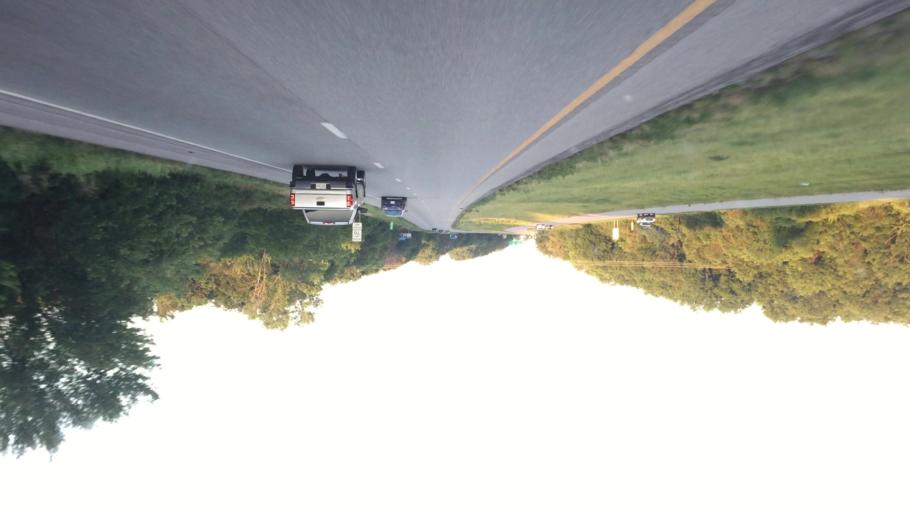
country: US
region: Missouri
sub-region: Clay County
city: Smithville
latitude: 39.3115
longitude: -94.5670
